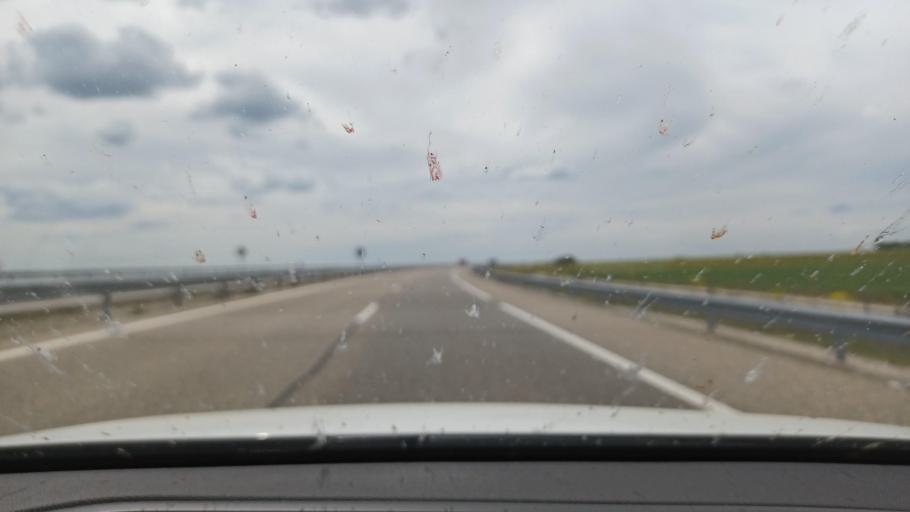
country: ES
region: Castille and Leon
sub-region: Provincia de Valladolid
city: San Miguel del Arroyo
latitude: 41.4341
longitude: -4.4324
